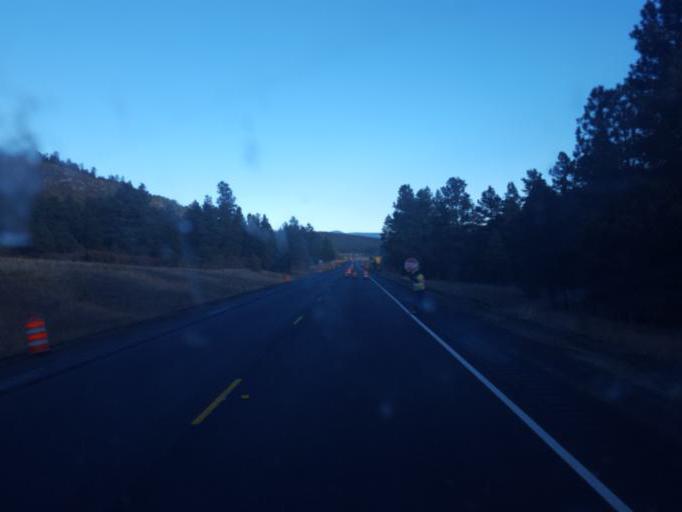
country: US
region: New Mexico
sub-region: Mora County
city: Mora
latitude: 35.8551
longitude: -105.2445
